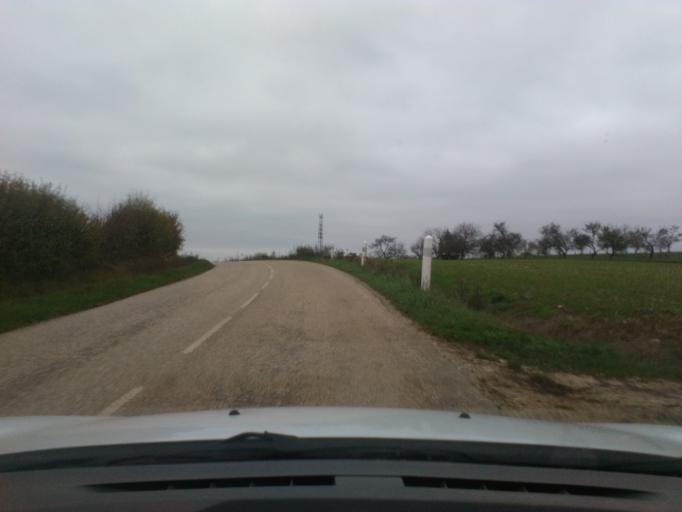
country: FR
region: Lorraine
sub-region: Departement des Vosges
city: Dogneville
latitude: 48.2790
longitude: 6.4826
